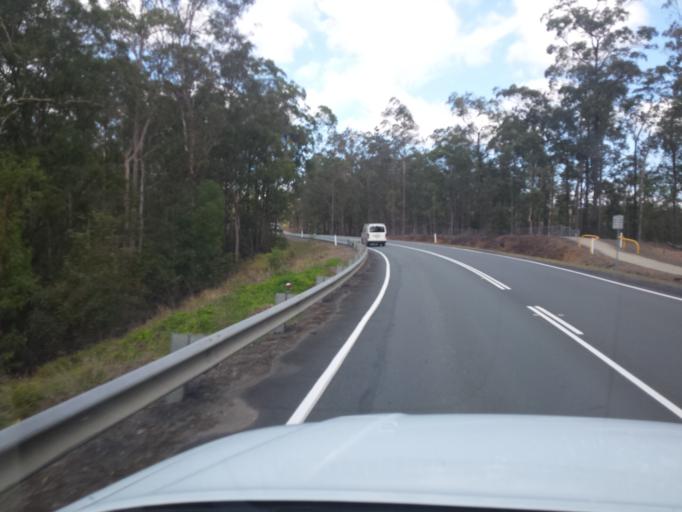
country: AU
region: Queensland
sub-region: Moreton Bay
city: Ferny Hills
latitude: -27.3739
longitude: 152.9583
